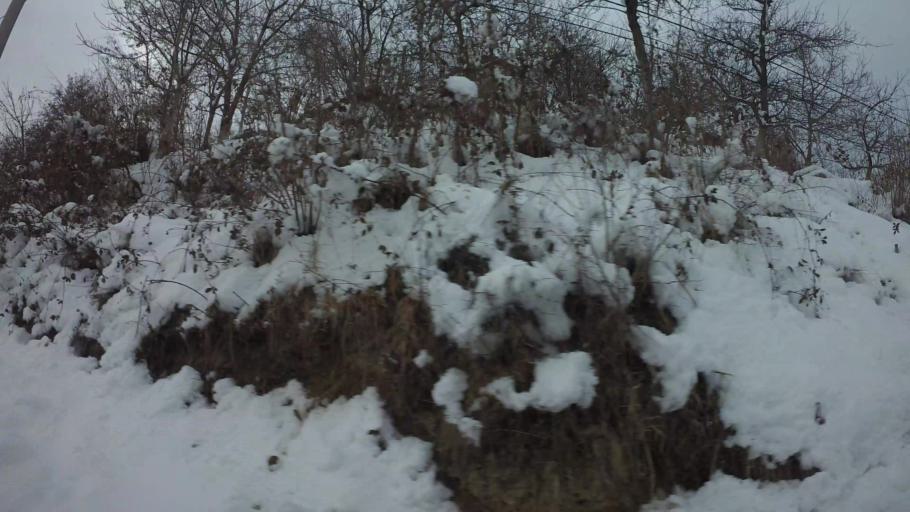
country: BA
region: Federation of Bosnia and Herzegovina
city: Kobilja Glava
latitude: 43.8717
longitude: 18.3889
